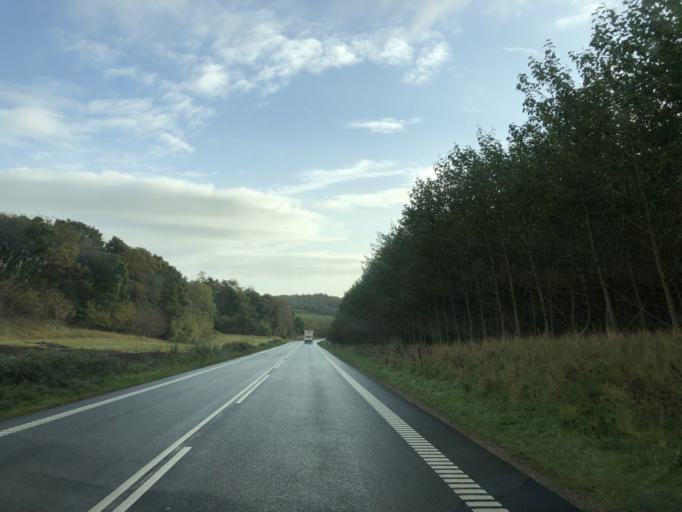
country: DK
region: North Denmark
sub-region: Mariagerfjord Kommune
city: Hobro
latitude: 56.6153
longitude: 9.6643
